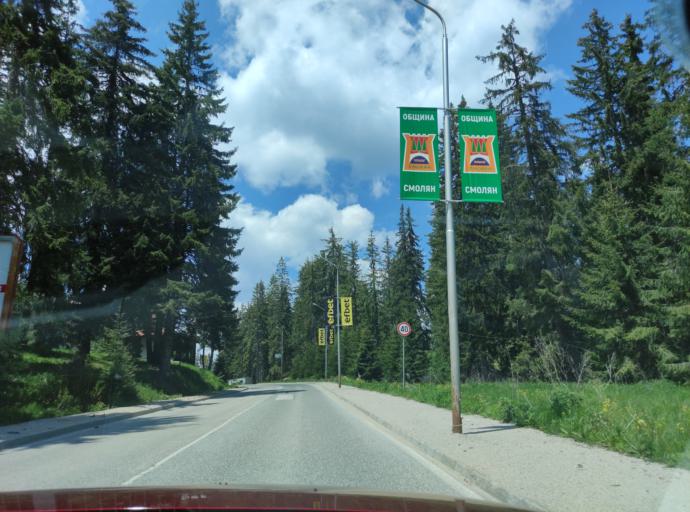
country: BG
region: Smolyan
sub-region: Obshtina Smolyan
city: Smolyan
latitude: 41.6383
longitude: 24.6988
